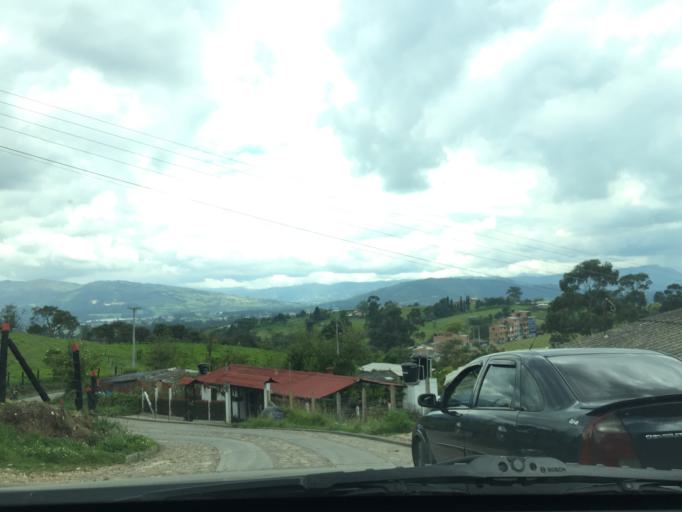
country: CO
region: Cundinamarca
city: Zipaquira
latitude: 5.0483
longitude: -74.0027
